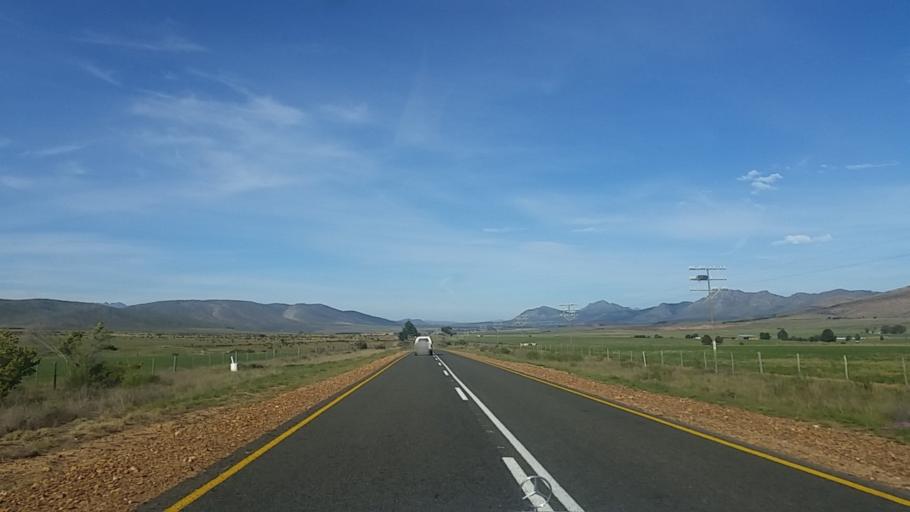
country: ZA
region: Western Cape
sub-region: Eden District Municipality
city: George
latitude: -33.8195
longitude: 22.4983
